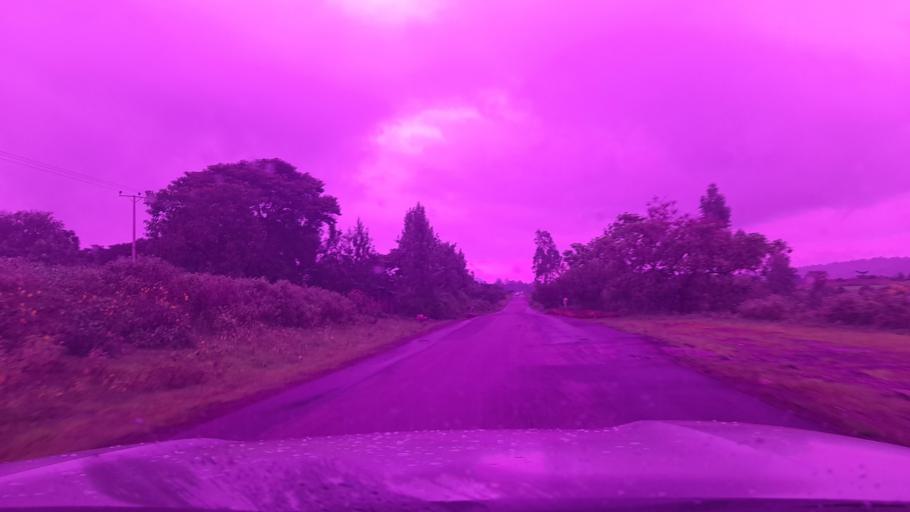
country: ET
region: Oromiya
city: Jima
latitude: 7.7821
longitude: 37.3424
